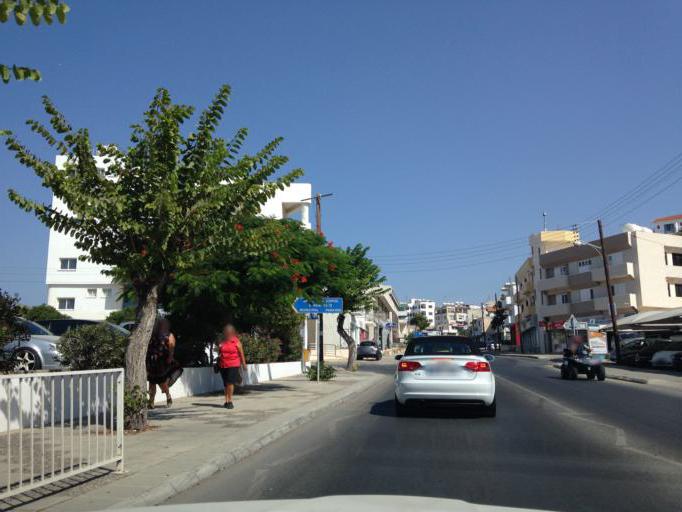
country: CY
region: Pafos
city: Paphos
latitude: 34.7724
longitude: 32.4184
